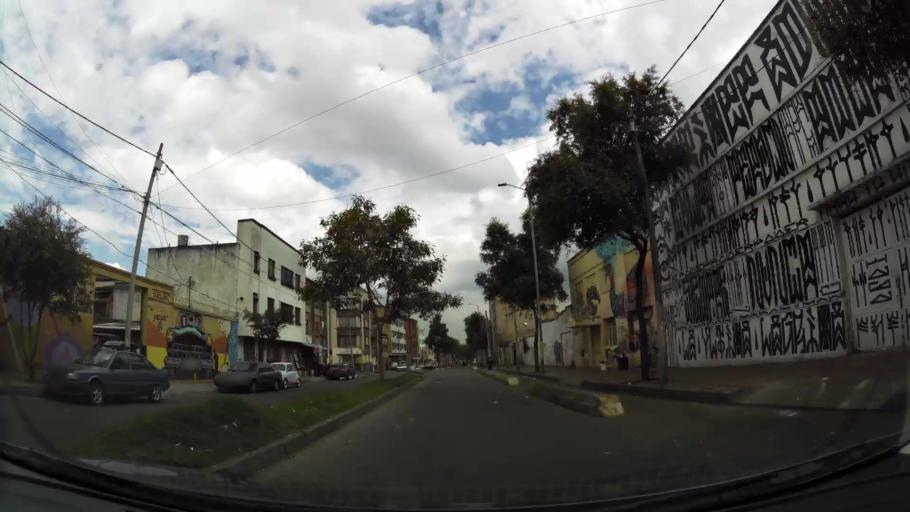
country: CO
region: Bogota D.C.
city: Bogota
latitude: 4.6150
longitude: -74.0761
